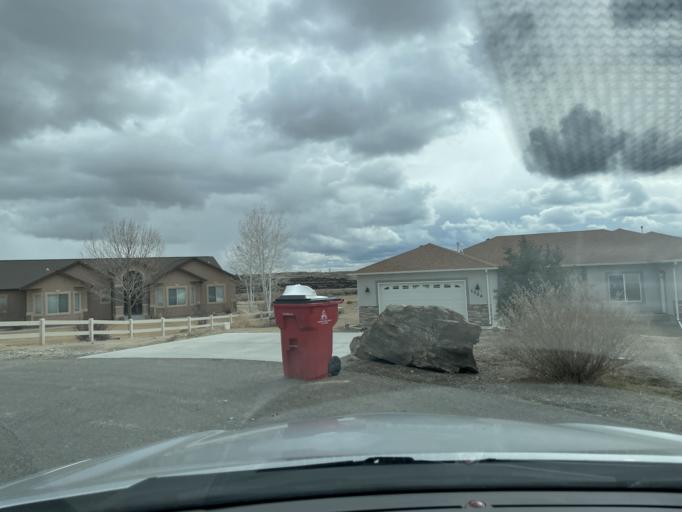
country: US
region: Colorado
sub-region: Mesa County
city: Loma
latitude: 39.2149
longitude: -108.8053
